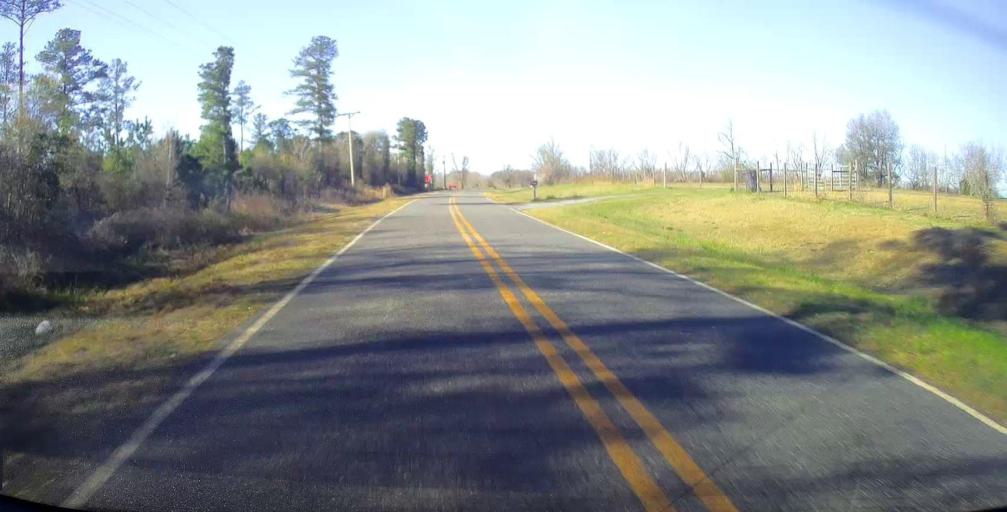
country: US
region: Georgia
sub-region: Peach County
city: Fort Valley
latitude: 32.5927
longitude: -83.8524
